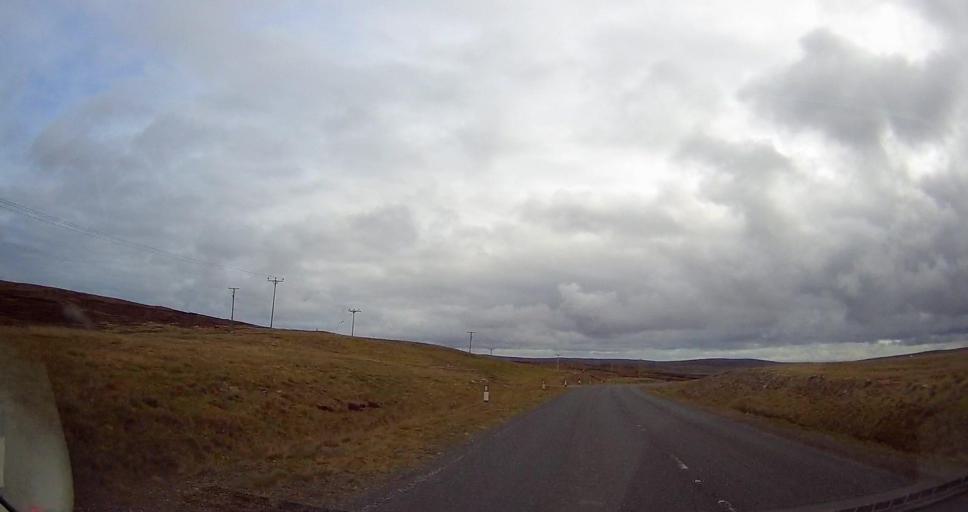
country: GB
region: Scotland
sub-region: Shetland Islands
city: Shetland
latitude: 60.5903
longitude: -1.1675
